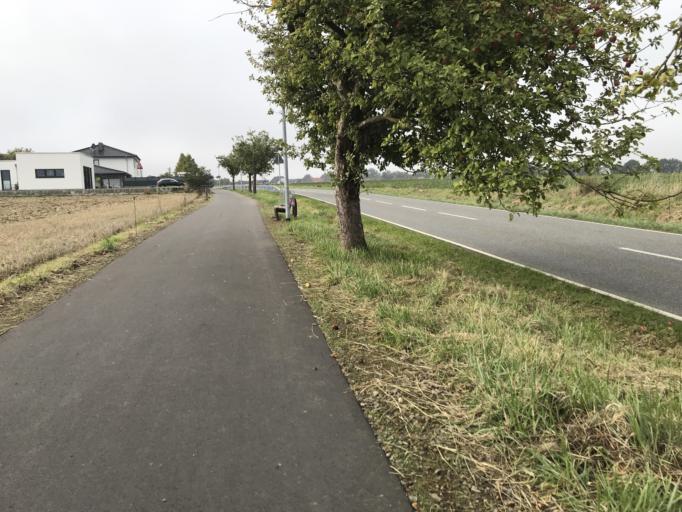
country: DE
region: Hesse
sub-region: Regierungsbezirk Kassel
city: Guxhagen
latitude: 51.2075
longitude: 9.4374
